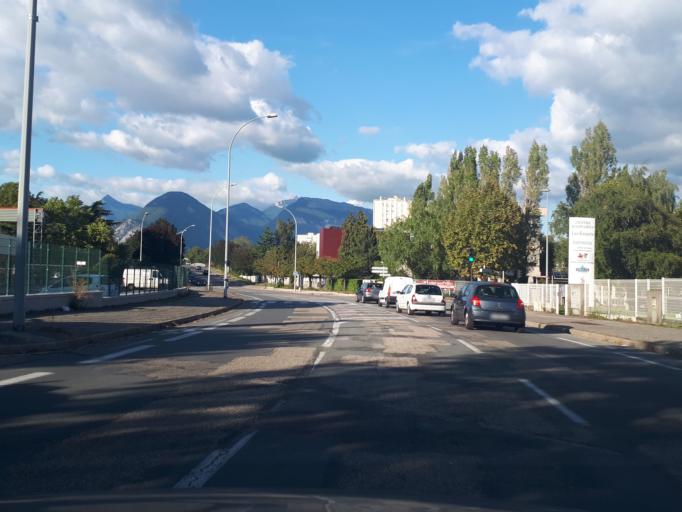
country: FR
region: Rhone-Alpes
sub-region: Departement de l'Isere
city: Grenoble
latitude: 45.1536
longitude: 5.7119
